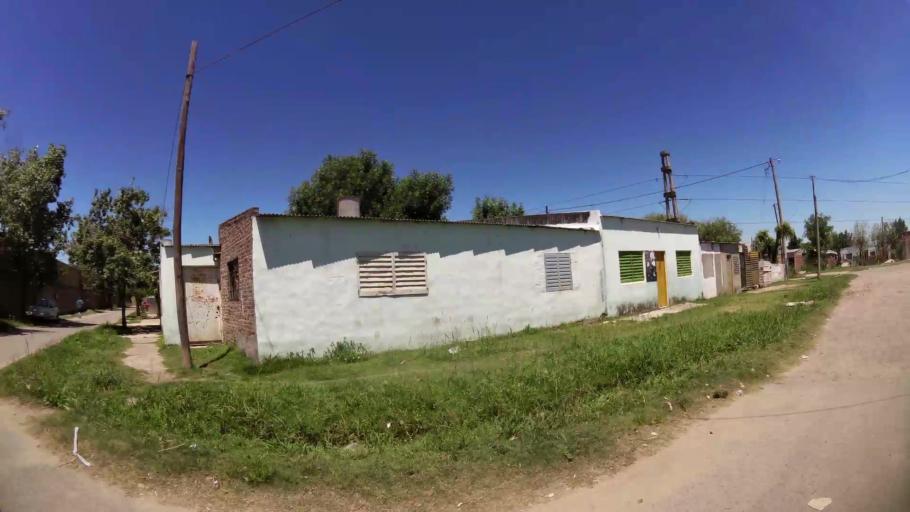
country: AR
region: Santa Fe
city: Santa Fe de la Vera Cruz
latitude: -31.6133
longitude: -60.7195
